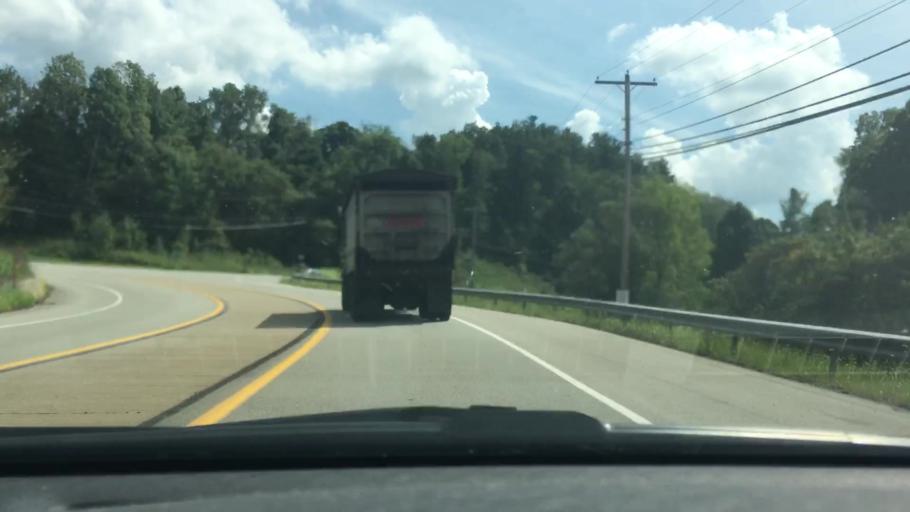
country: US
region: Pennsylvania
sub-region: Washington County
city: Gastonville
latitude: 40.2536
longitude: -79.9854
